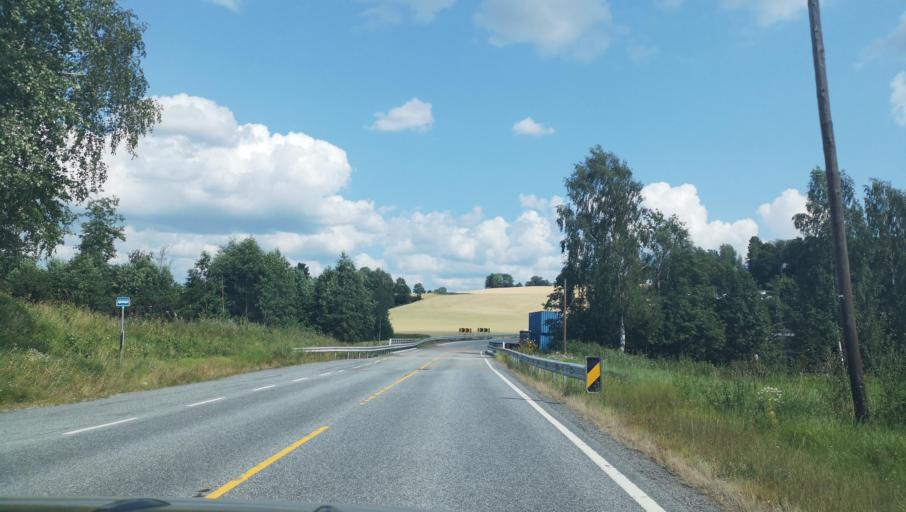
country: NO
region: Buskerud
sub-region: Ovre Eiker
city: Hokksund
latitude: 59.7253
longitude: 9.8336
